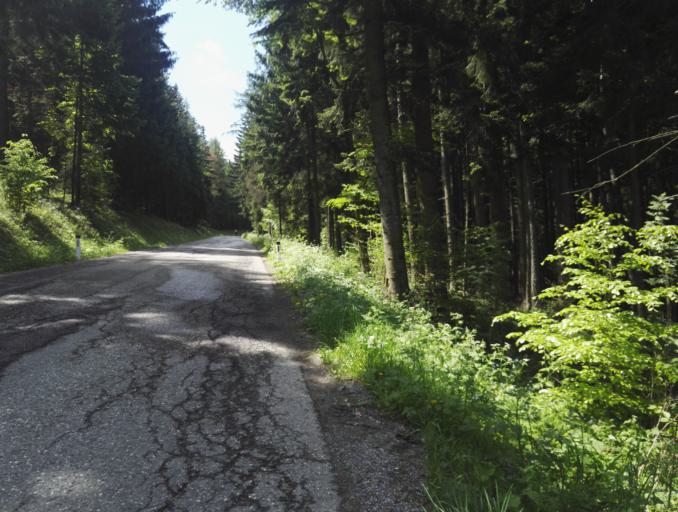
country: AT
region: Styria
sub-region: Politischer Bezirk Weiz
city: Stenzengreith
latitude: 47.2100
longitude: 15.4898
